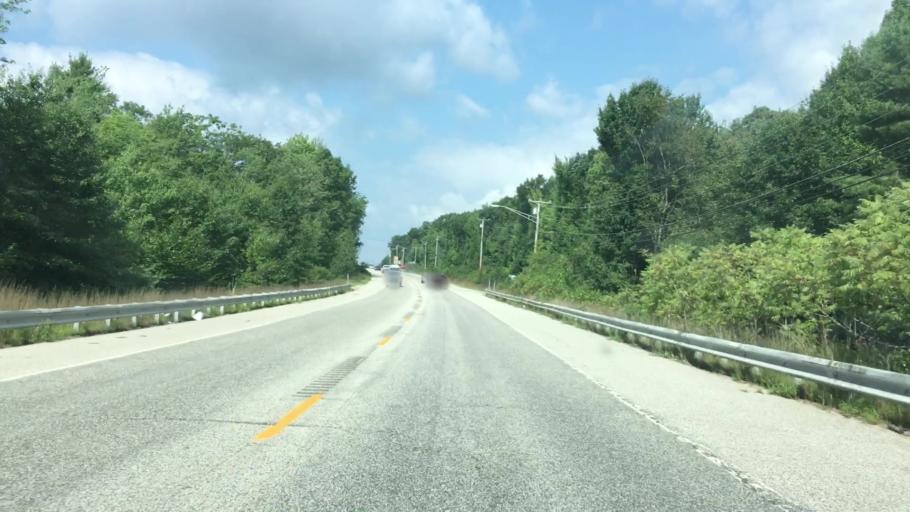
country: US
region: Maine
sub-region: Cumberland County
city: Raymond
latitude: 43.9084
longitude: -70.4930
